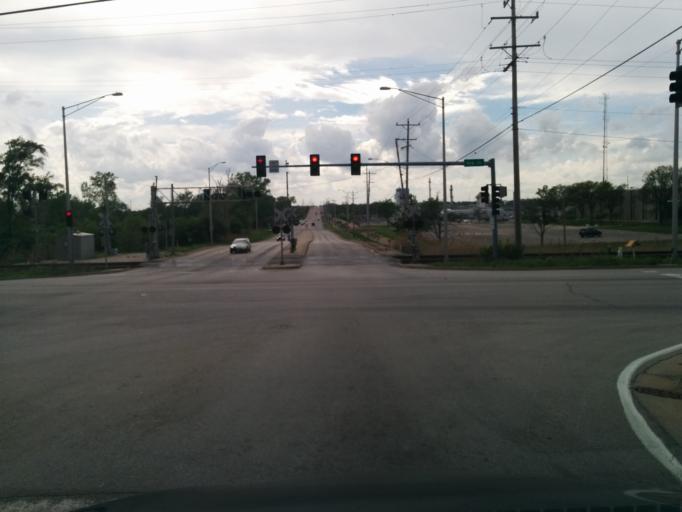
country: US
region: Illinois
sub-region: Will County
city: Romeoville
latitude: 41.6410
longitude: -88.0484
